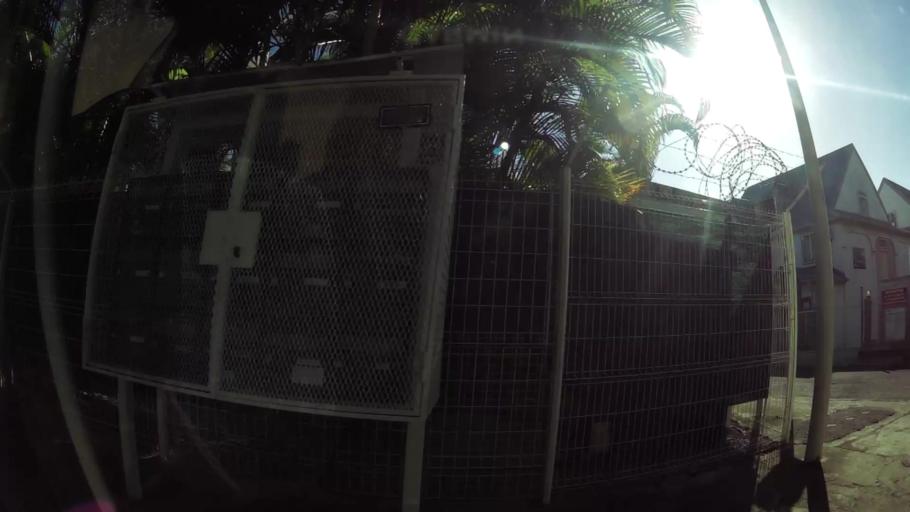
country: GP
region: Guadeloupe
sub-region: Guadeloupe
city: Le Gosier
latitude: 16.2025
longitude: -61.4730
